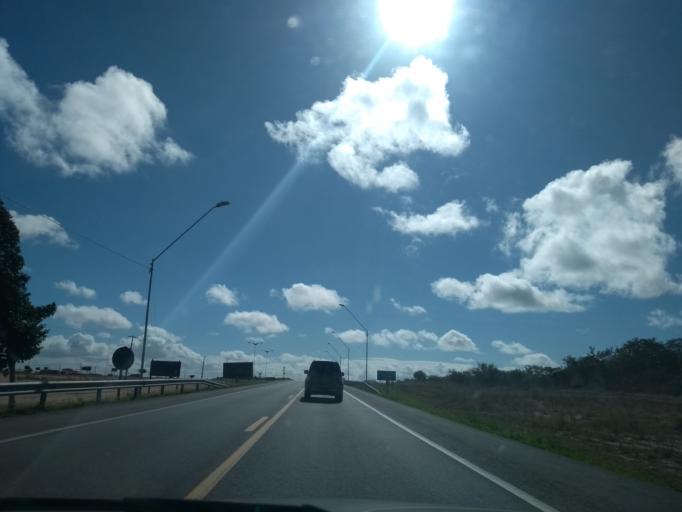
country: BR
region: Bahia
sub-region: Amargosa
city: Amargosa
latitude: -12.8616
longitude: -39.8517
